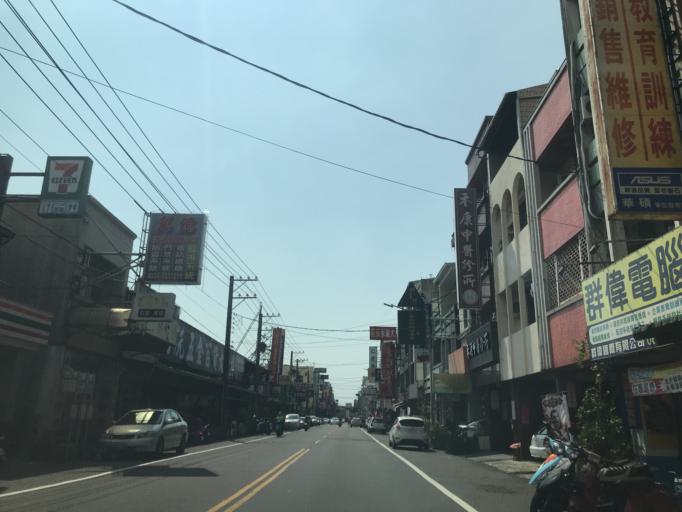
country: TW
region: Taiwan
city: Yujing
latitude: 23.1329
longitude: 120.3020
